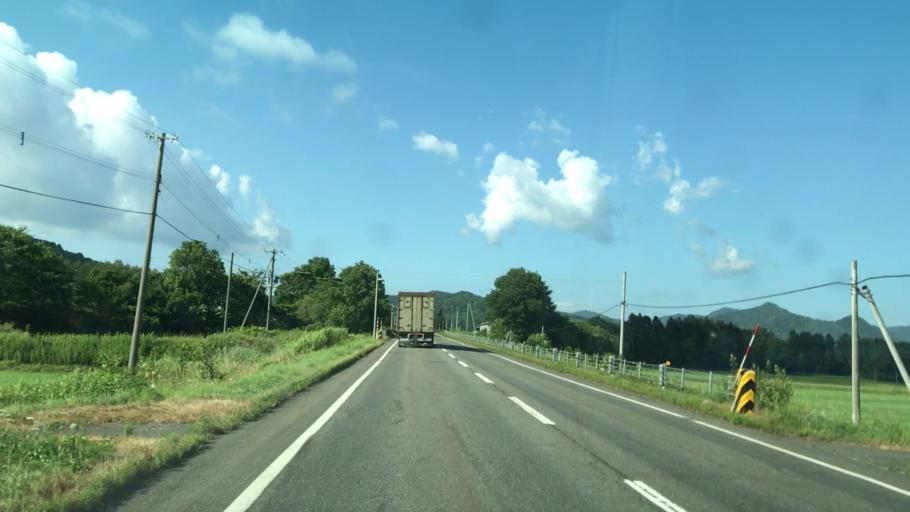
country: JP
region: Hokkaido
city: Shimo-furano
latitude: 42.8687
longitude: 142.4265
